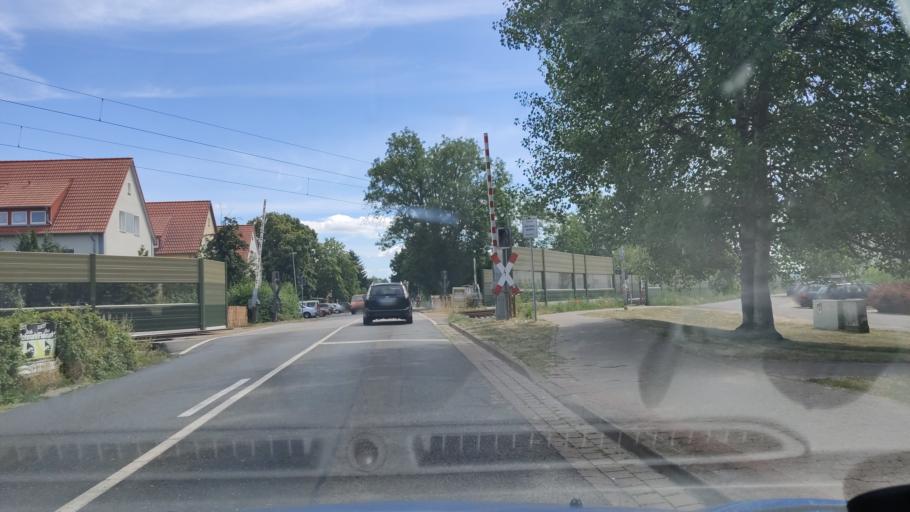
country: DE
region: Lower Saxony
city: Ronnenberg
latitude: 52.3367
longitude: 9.6652
